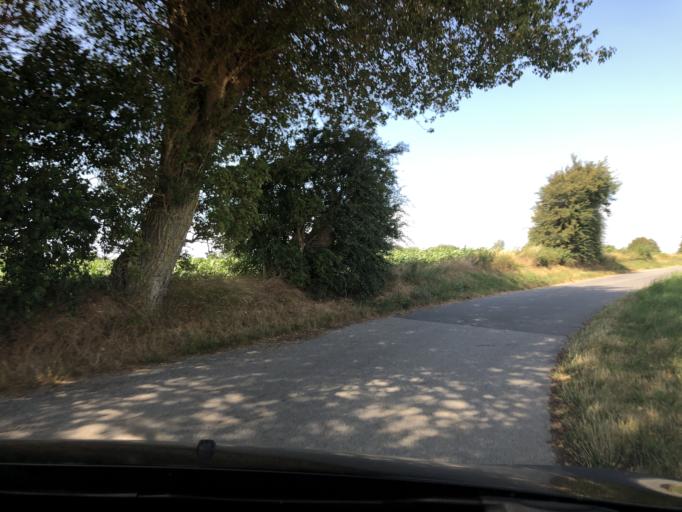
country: DK
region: South Denmark
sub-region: AEro Kommune
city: AEroskobing
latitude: 54.9053
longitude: 10.2744
